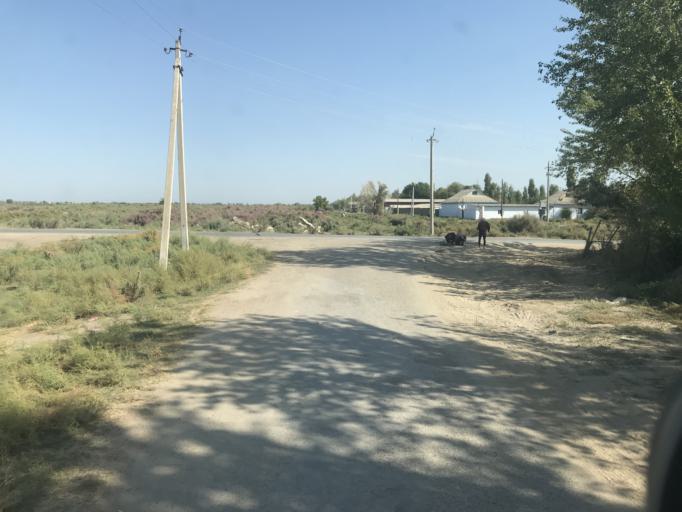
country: KZ
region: Ongtustik Qazaqstan
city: Myrzakent
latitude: 40.6641
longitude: 68.6134
